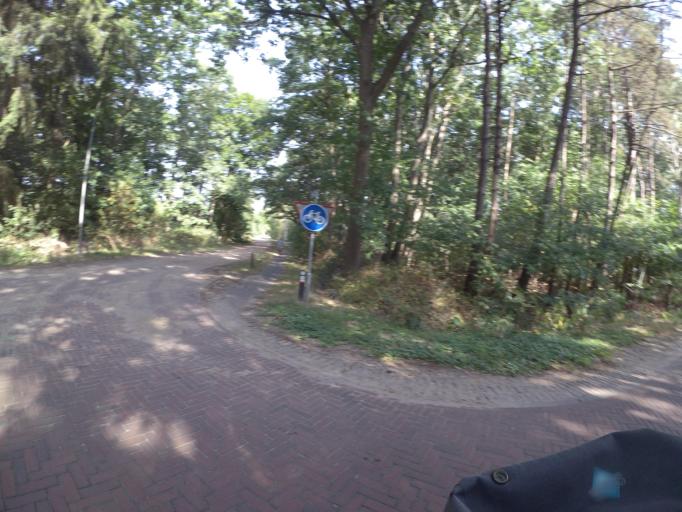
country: NL
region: Drenthe
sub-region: Gemeente Westerveld
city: Havelte
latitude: 52.7724
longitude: 6.2090
